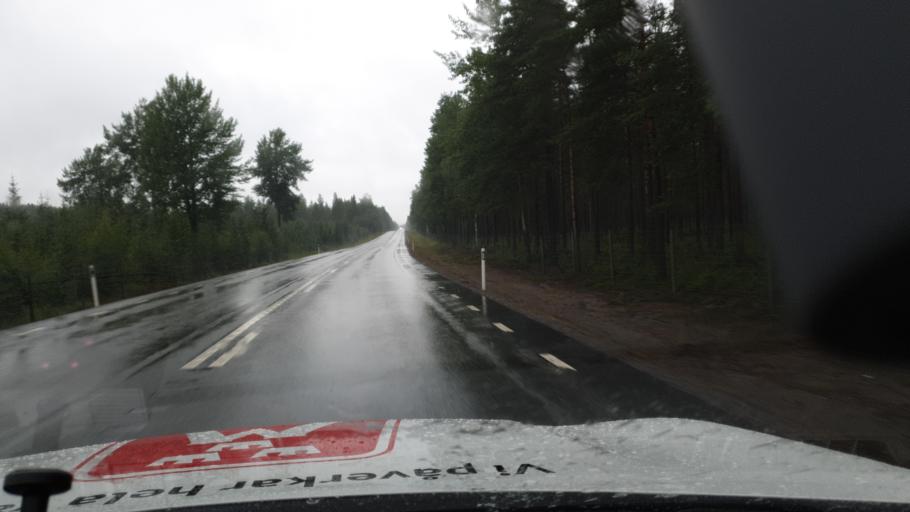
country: SE
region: Vaesterbotten
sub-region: Skelleftea Kommun
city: Burea
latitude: 64.5682
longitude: 21.2274
